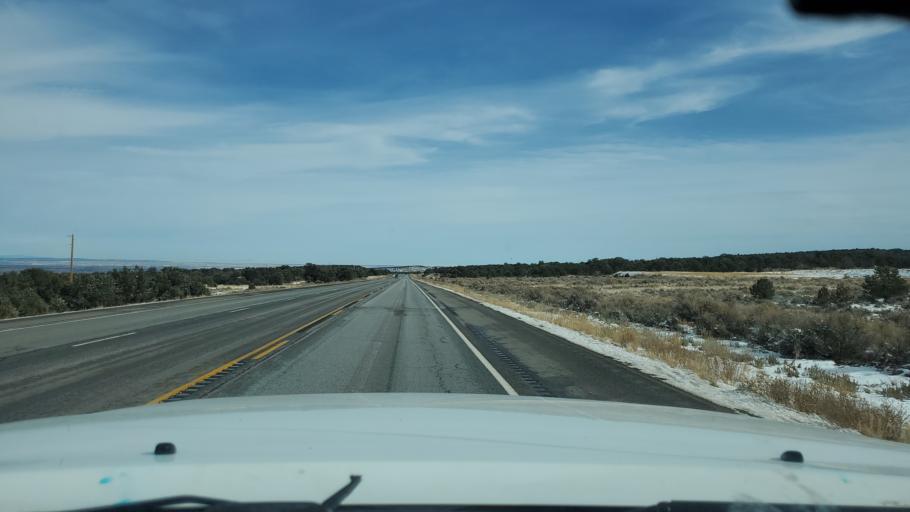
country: US
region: Utah
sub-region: Duchesne County
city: Duchesne
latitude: 40.1814
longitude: -110.6440
